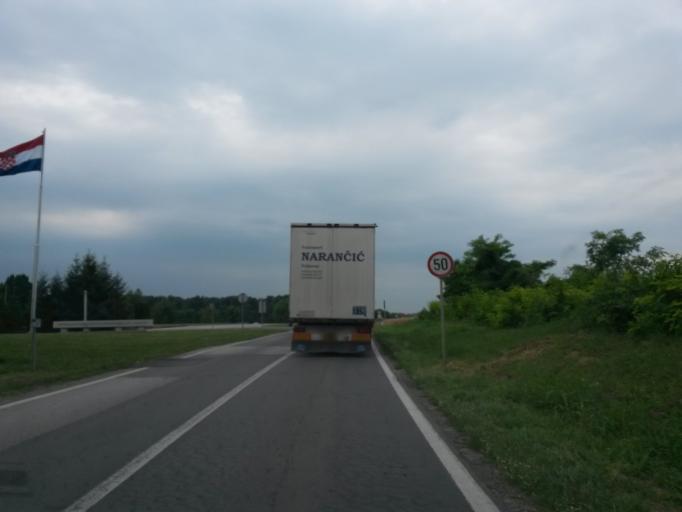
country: HR
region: Vukovarsko-Srijemska
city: Vukovar
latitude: 45.3305
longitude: 19.0404
